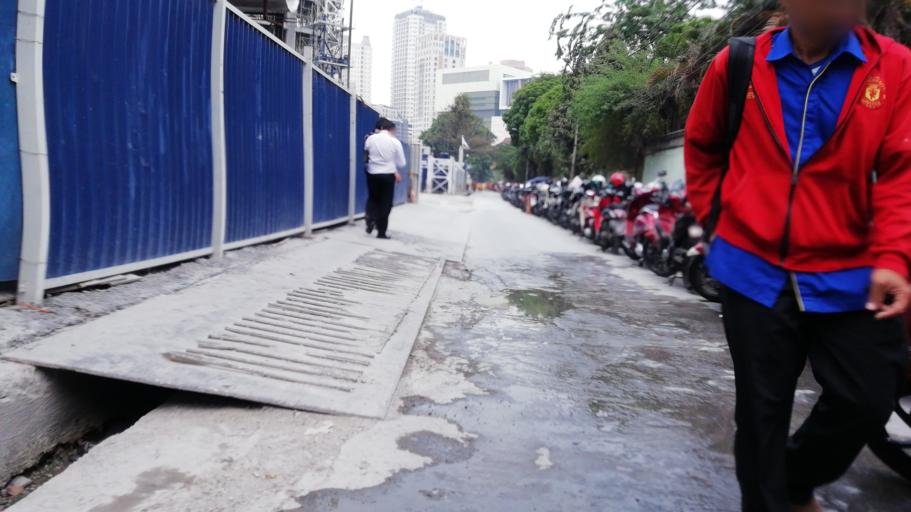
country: ID
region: Jakarta Raya
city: Jakarta
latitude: -6.1985
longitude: 106.8219
